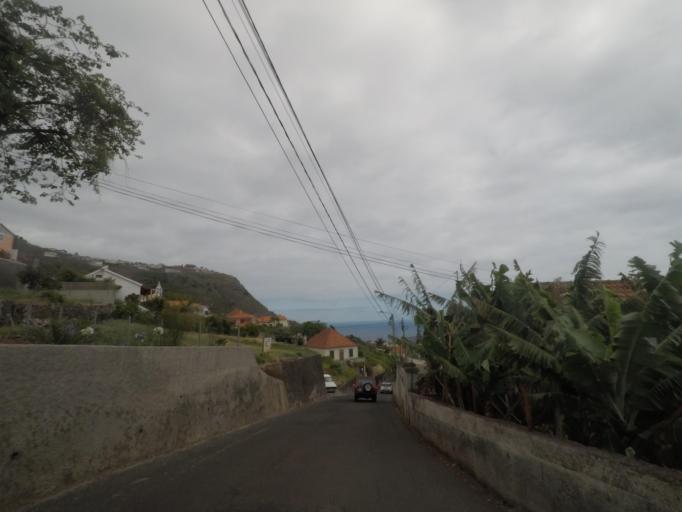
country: PT
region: Madeira
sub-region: Calheta
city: Arco da Calheta
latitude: 32.7166
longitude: -17.1472
